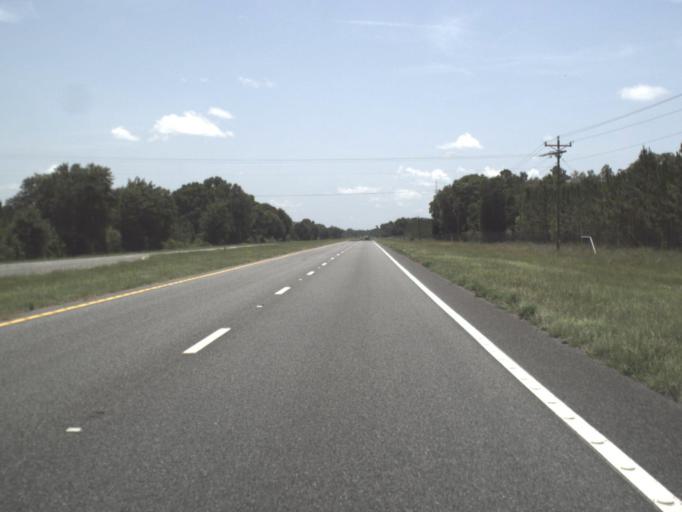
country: US
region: Florida
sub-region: Taylor County
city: Steinhatchee
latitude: 29.7922
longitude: -83.3342
